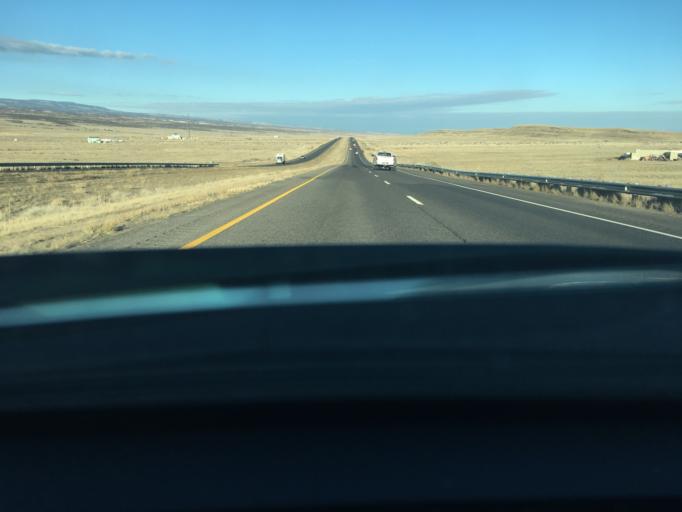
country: US
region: Colorado
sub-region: Mesa County
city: Palisade
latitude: 38.8661
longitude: -108.3286
